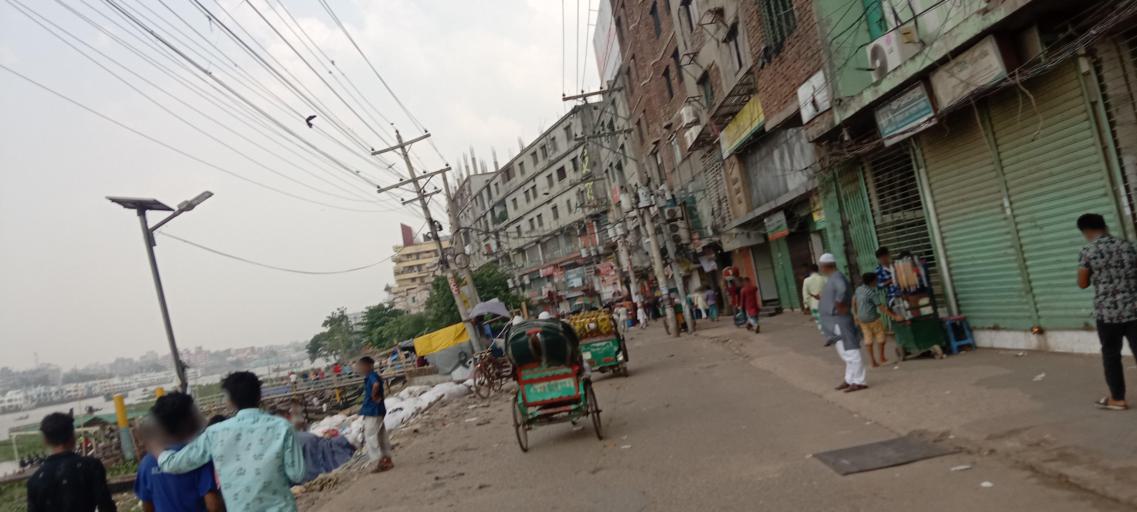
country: BD
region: Dhaka
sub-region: Dhaka
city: Dhaka
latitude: 23.7054
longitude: 90.4045
